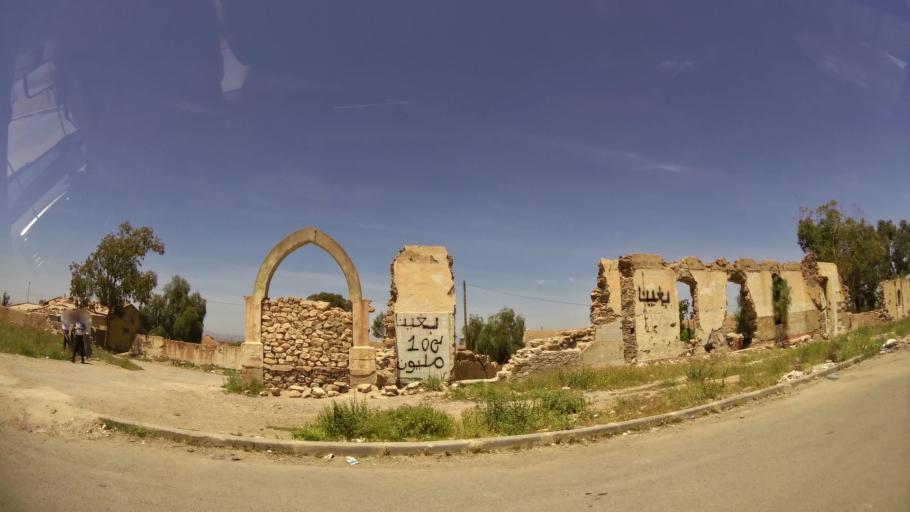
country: MA
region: Oriental
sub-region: Oujda-Angad
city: Oujda
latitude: 34.6663
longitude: -1.9209
